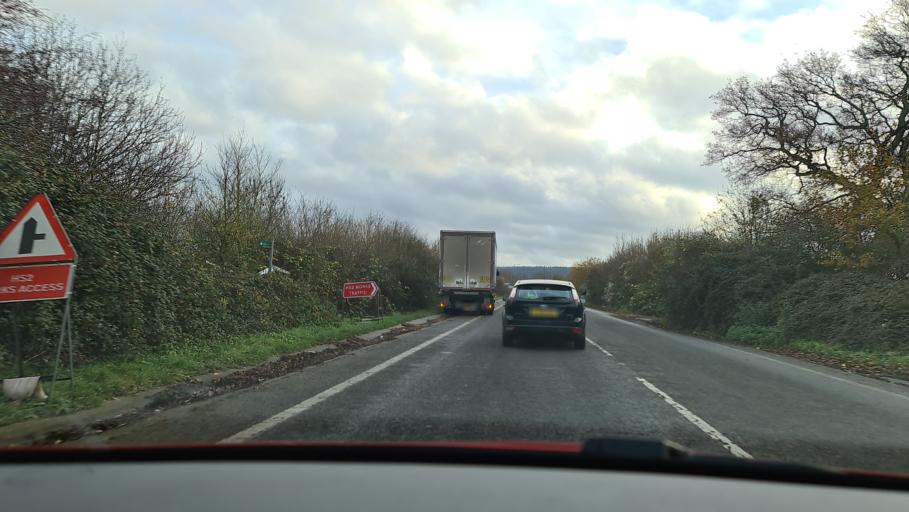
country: GB
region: England
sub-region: Buckinghamshire
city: Weston Turville
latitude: 51.7704
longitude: -0.7702
